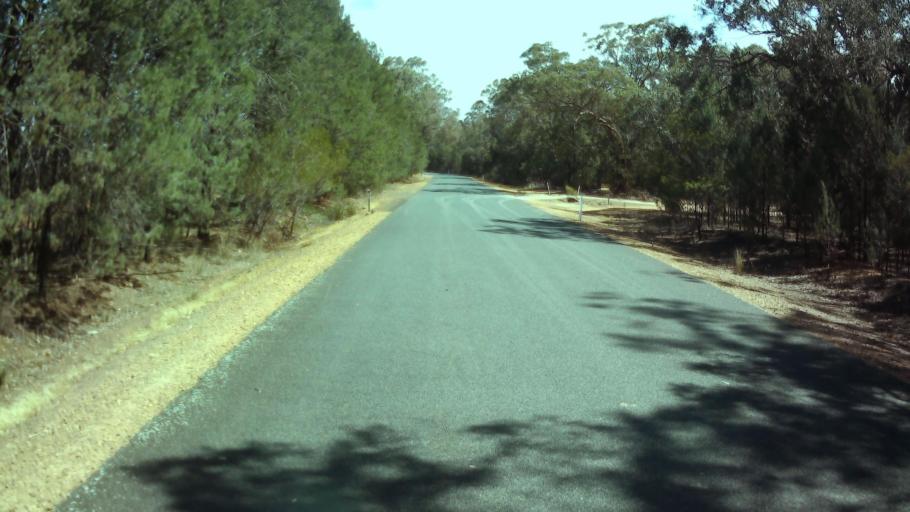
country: AU
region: New South Wales
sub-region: Weddin
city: Grenfell
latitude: -34.0115
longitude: 148.1296
